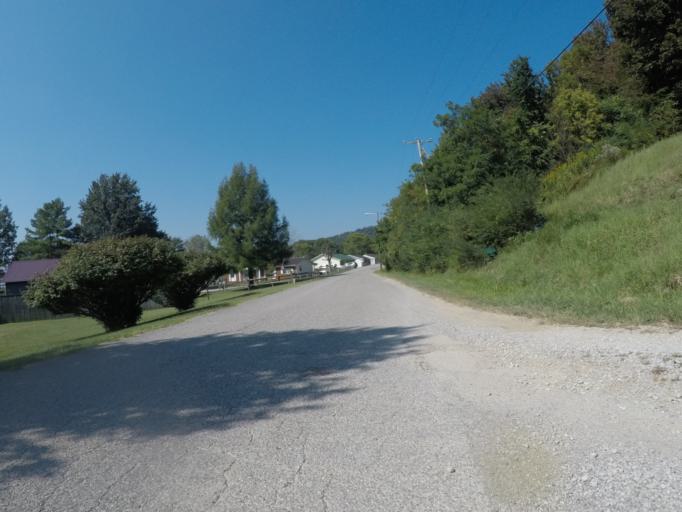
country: US
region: West Virginia
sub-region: Cabell County
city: Barboursville
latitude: 38.3708
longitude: -82.2720
